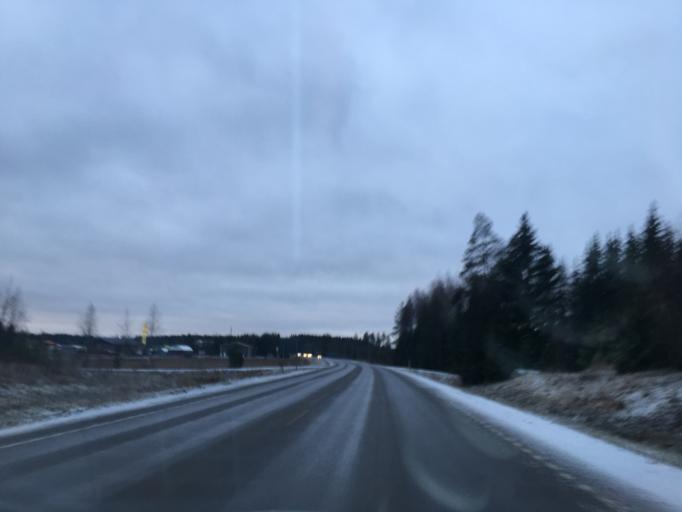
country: FI
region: Varsinais-Suomi
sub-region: Loimaa
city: Aura
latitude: 60.6465
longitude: 22.5496
